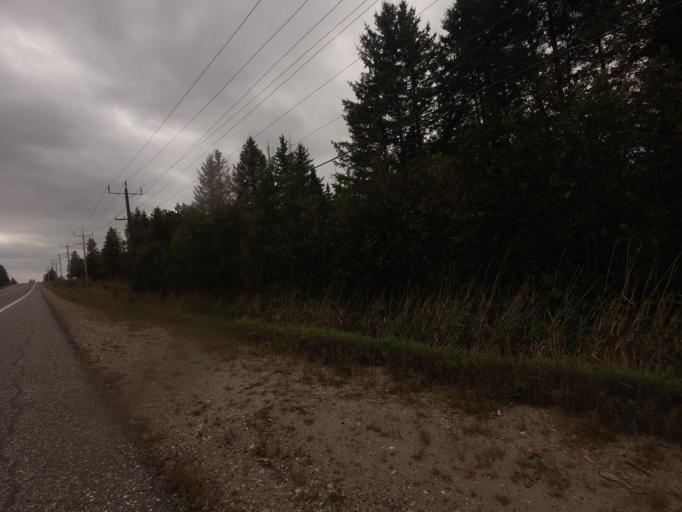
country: CA
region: Quebec
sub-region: Outaouais
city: Wakefield
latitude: 45.9219
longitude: -76.0172
